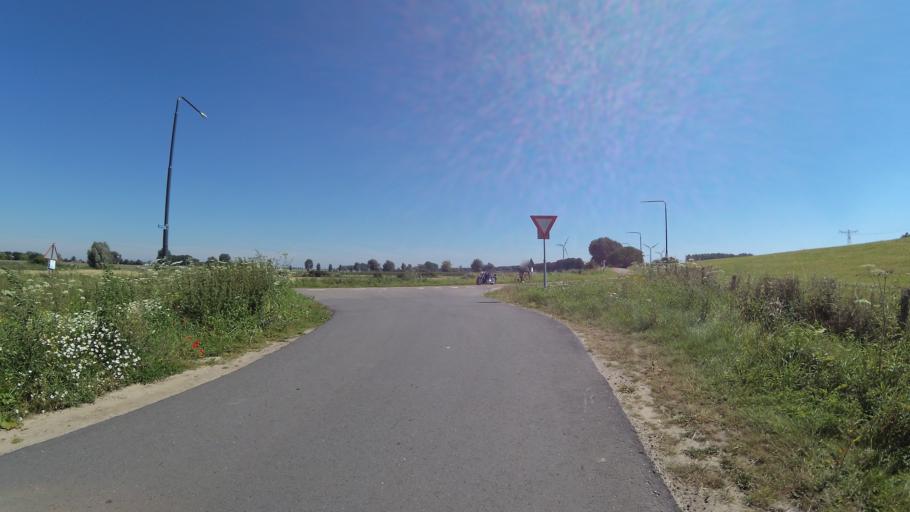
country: NL
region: North Brabant
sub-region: Gemeente Waalwijk
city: Waalwijk
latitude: 51.7080
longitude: 5.0502
